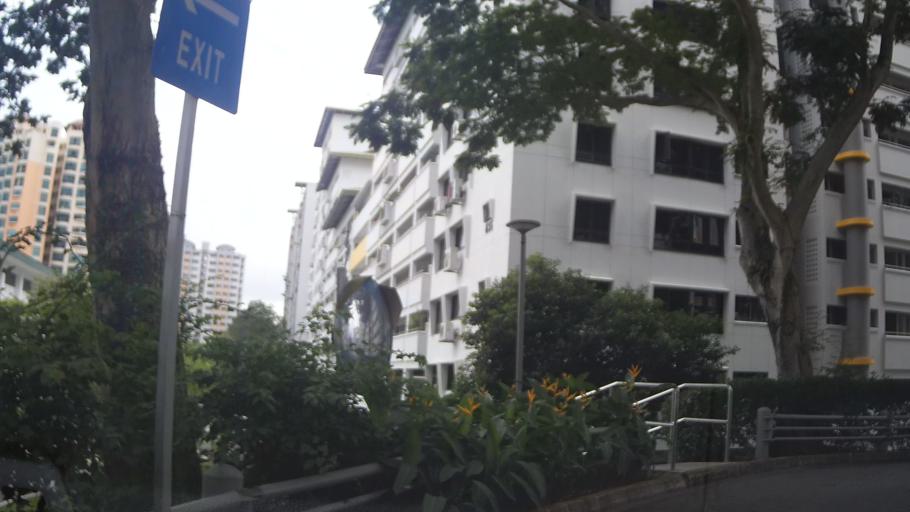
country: MY
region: Johor
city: Johor Bahru
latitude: 1.3977
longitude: 103.7500
